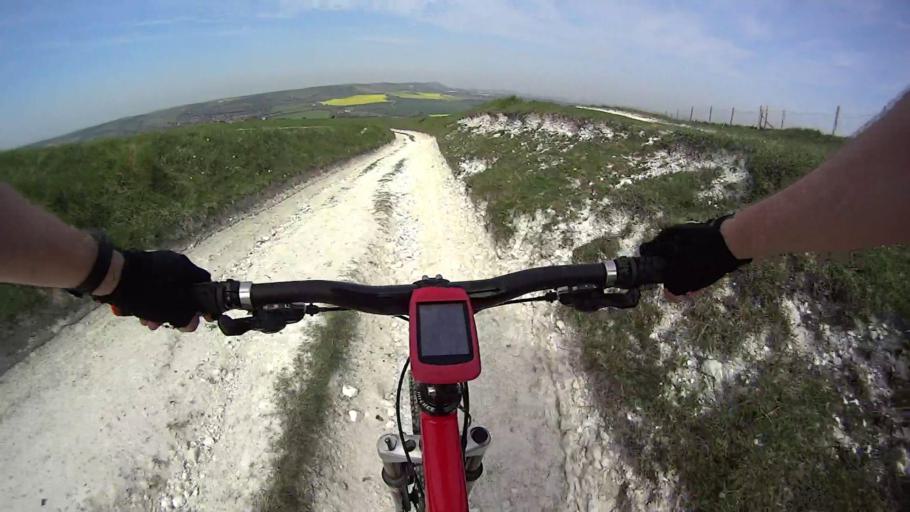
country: GB
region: England
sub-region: East Sussex
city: Hailsham
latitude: 50.8107
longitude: 0.1838
